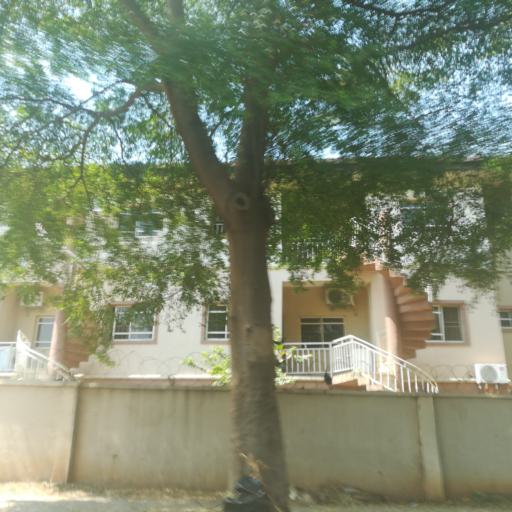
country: NG
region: Abuja Federal Capital Territory
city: Abuja
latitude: 9.0720
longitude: 7.4463
